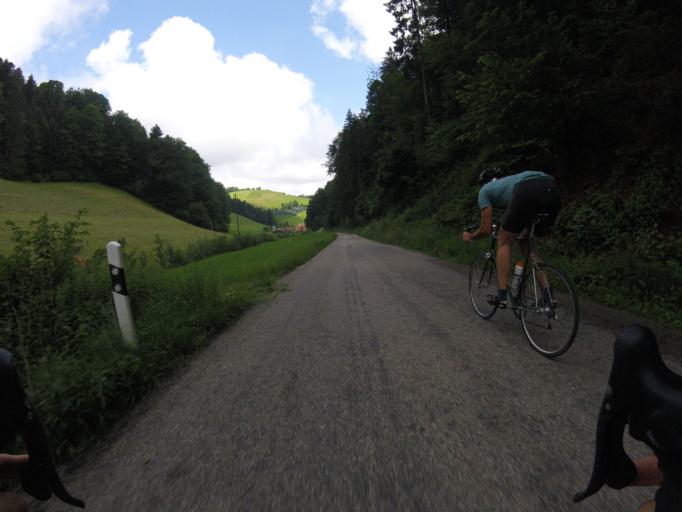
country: CH
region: Bern
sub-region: Emmental District
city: Krauchthal
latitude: 46.9855
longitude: 7.5829
